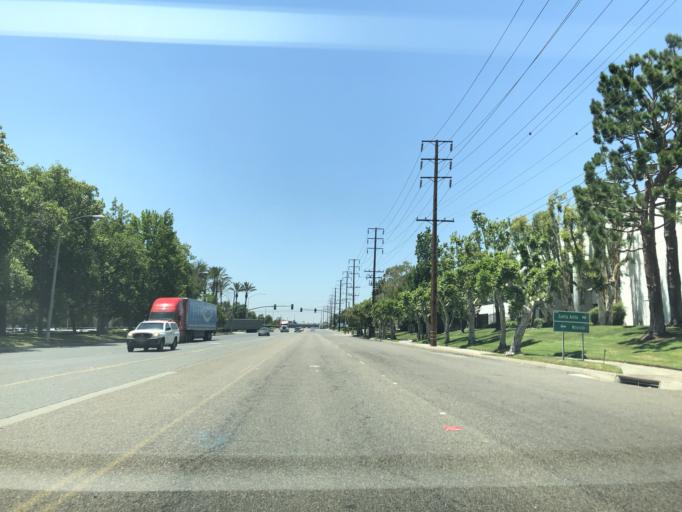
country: US
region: California
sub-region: San Bernardino County
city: Rancho Cucamonga
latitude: 34.0772
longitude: -117.5374
